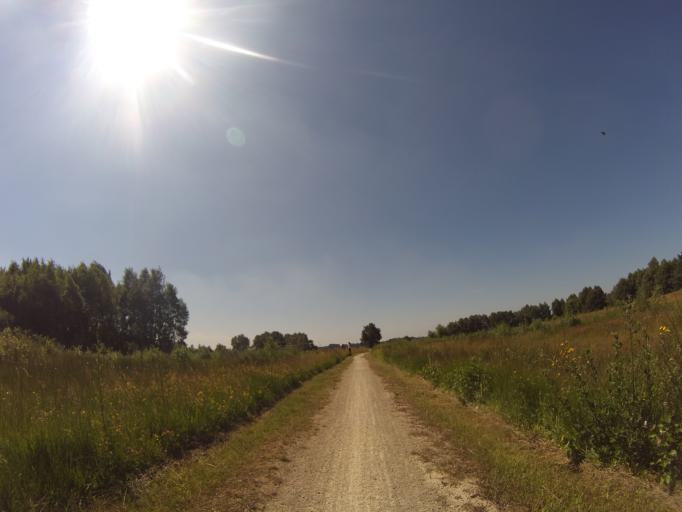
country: DE
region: Lower Saxony
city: Twist
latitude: 52.6579
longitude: 7.0121
